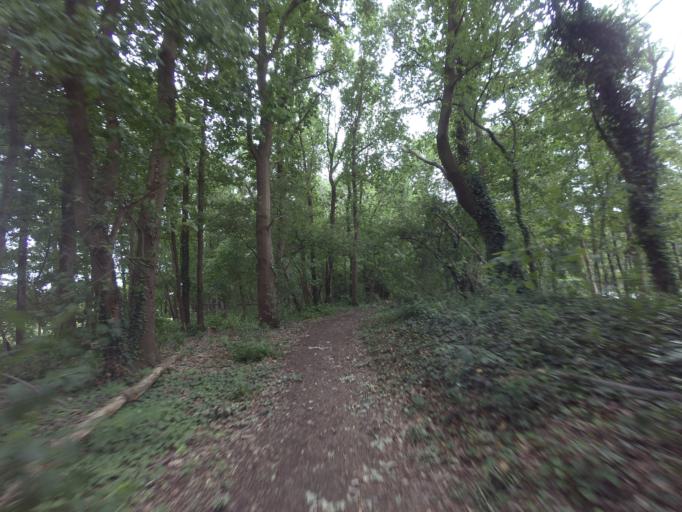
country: BE
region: Flanders
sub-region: Provincie Antwerpen
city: Mechelen
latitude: 51.0631
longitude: 4.4646
